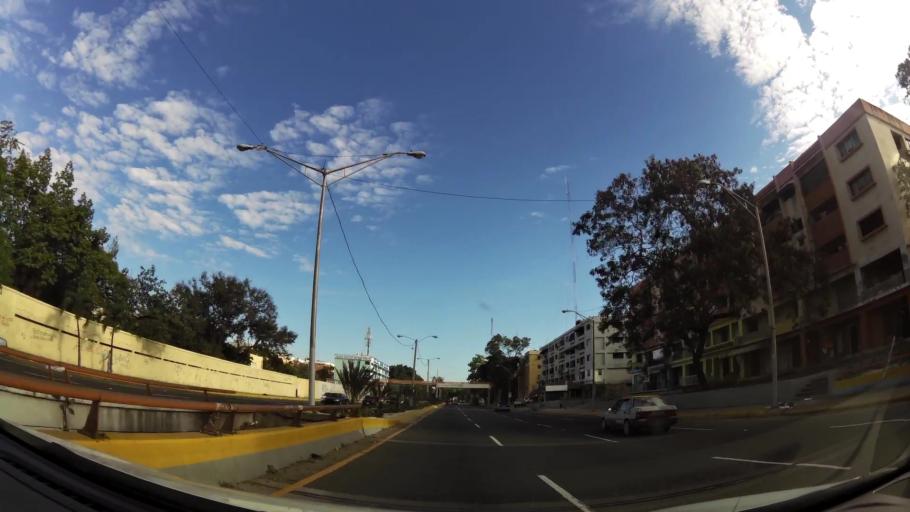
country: DO
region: Nacional
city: San Carlos
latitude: 18.4865
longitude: -69.9043
